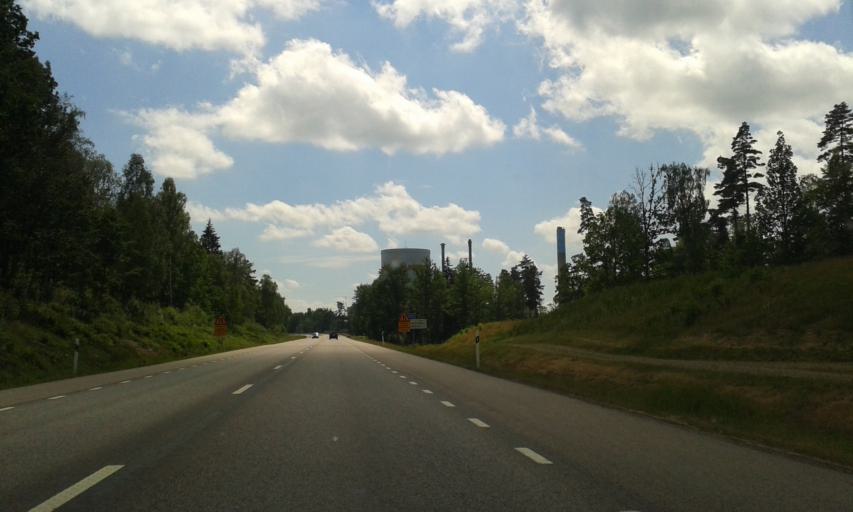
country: SE
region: Kronoberg
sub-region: Vaxjo Kommun
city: Vaexjoe
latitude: 56.8735
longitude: 14.8374
